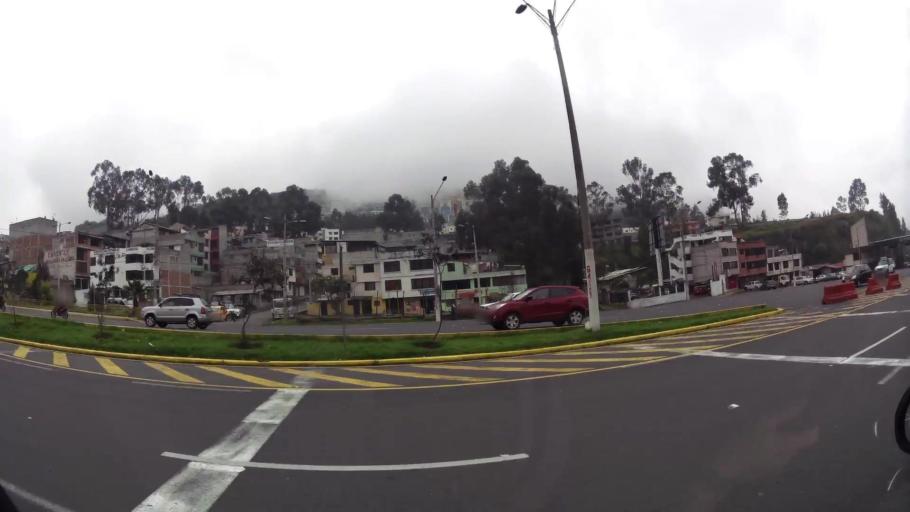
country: EC
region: Pichincha
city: Quito
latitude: -0.2427
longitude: -78.4856
